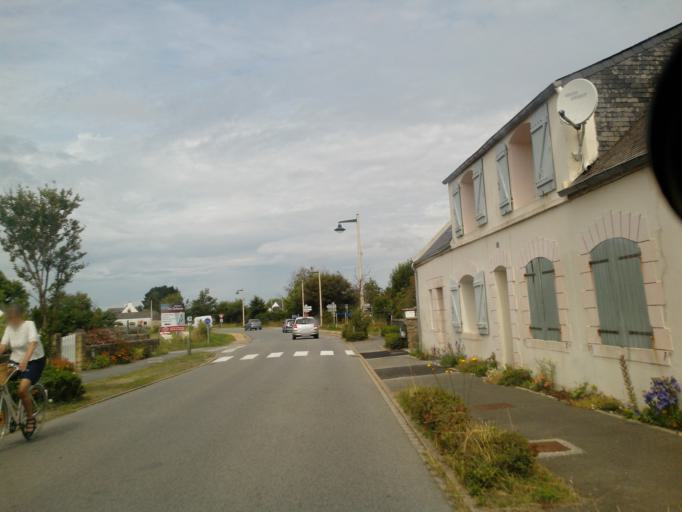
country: FR
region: Brittany
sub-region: Departement du Morbihan
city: Erdeven
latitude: 47.6419
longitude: -3.1497
